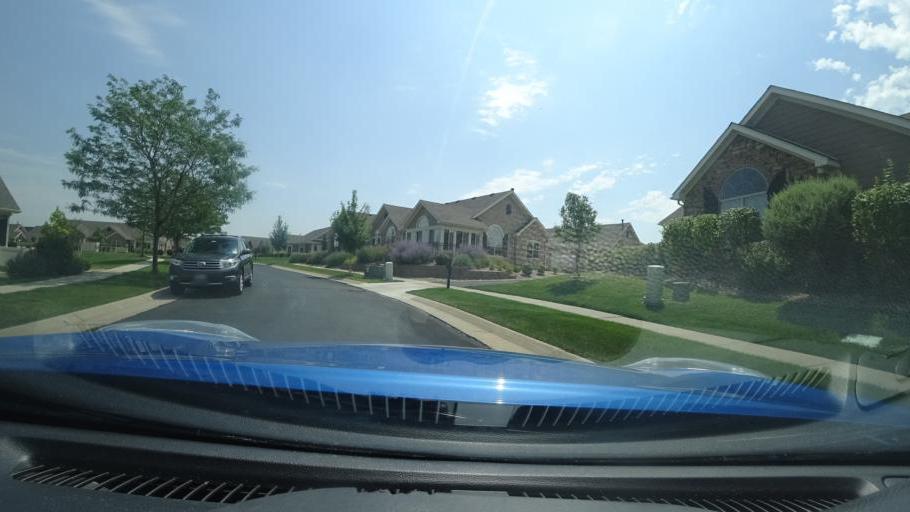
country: US
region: Colorado
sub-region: Adams County
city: Aurora
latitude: 39.6797
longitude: -104.7614
